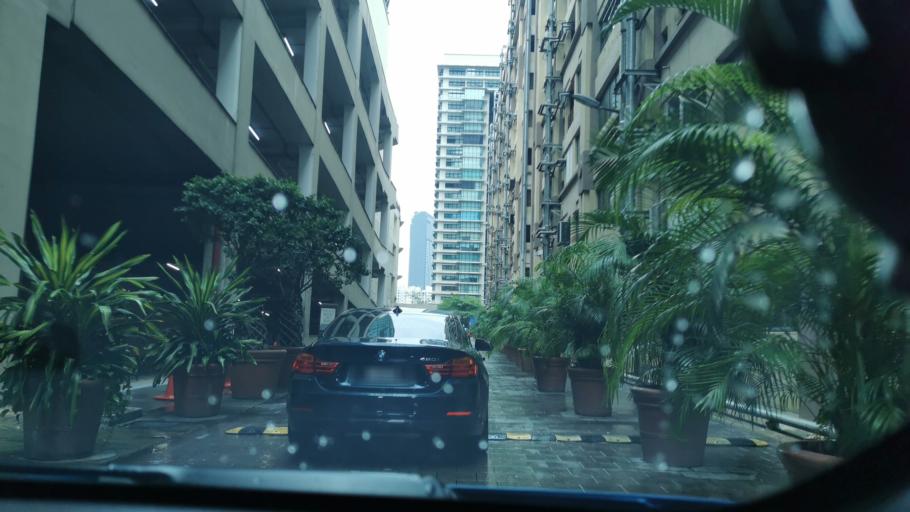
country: MY
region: Kuala Lumpur
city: Kuala Lumpur
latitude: 3.1186
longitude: 101.6764
